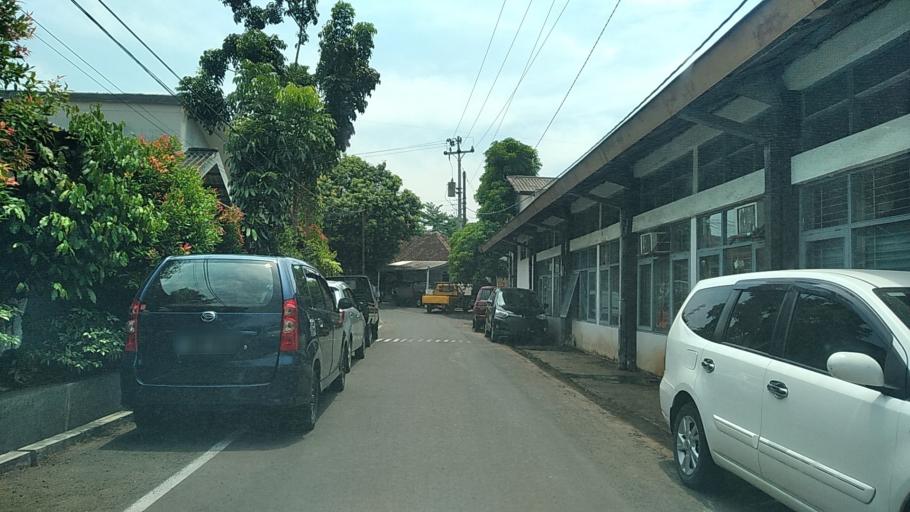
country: ID
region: Central Java
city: Semarang
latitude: -7.0582
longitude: 110.4185
